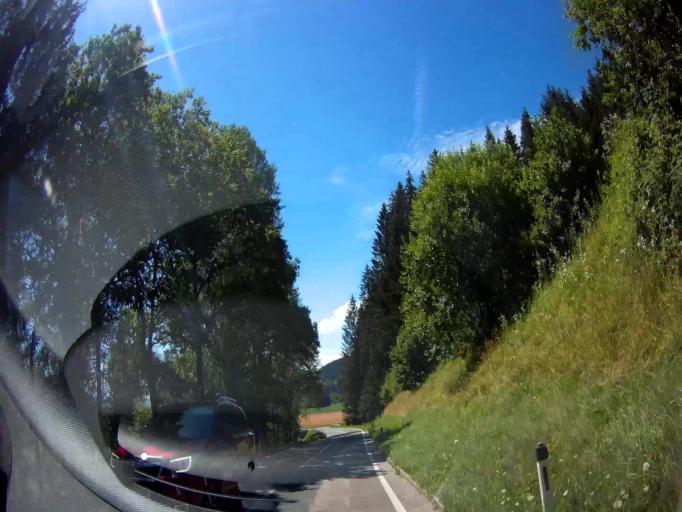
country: AT
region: Carinthia
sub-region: Politischer Bezirk Sankt Veit an der Glan
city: Glodnitz
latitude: 46.8525
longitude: 14.1841
